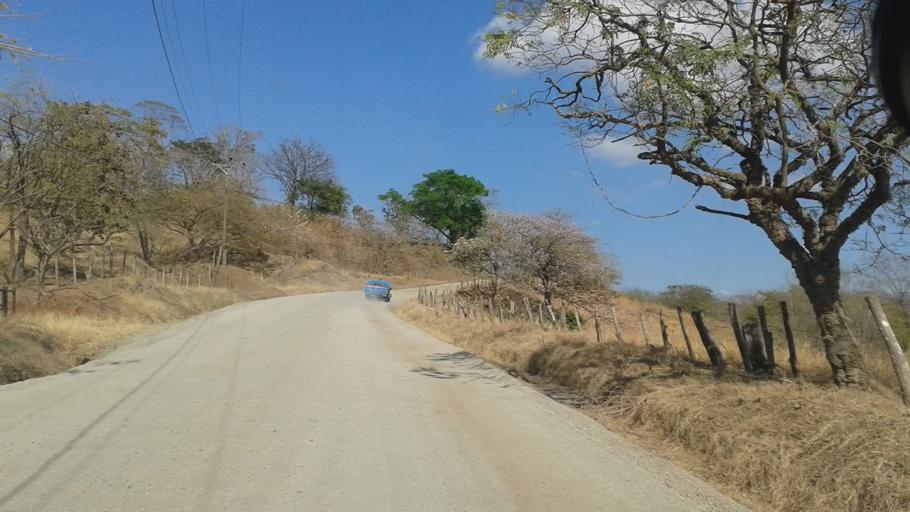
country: CR
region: Guanacaste
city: Santa Cruz
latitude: 10.1138
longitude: -85.7804
